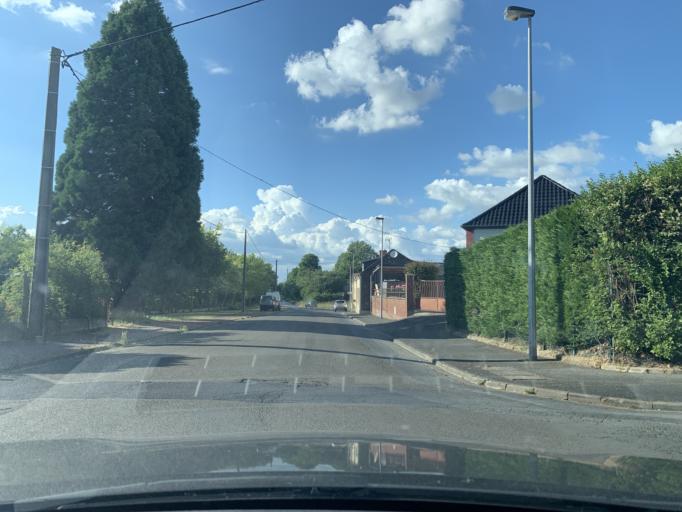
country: FR
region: Nord-Pas-de-Calais
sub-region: Departement du Nord
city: Cambrai
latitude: 50.1724
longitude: 3.2580
